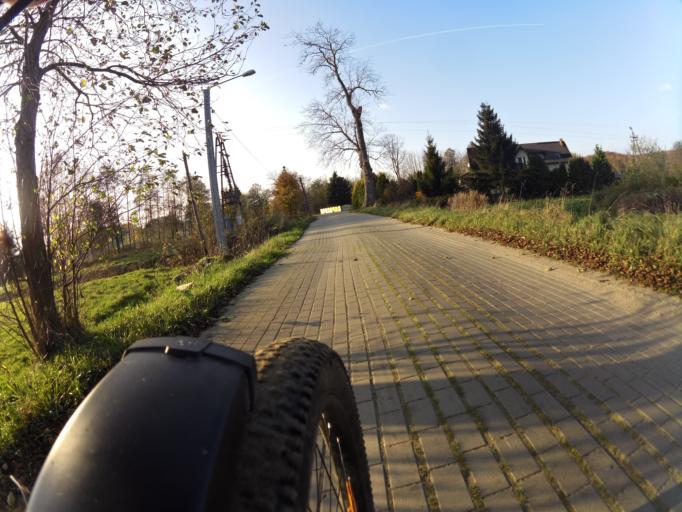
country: PL
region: Pomeranian Voivodeship
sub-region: Powiat pucki
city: Krokowa
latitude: 54.7501
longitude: 18.1934
